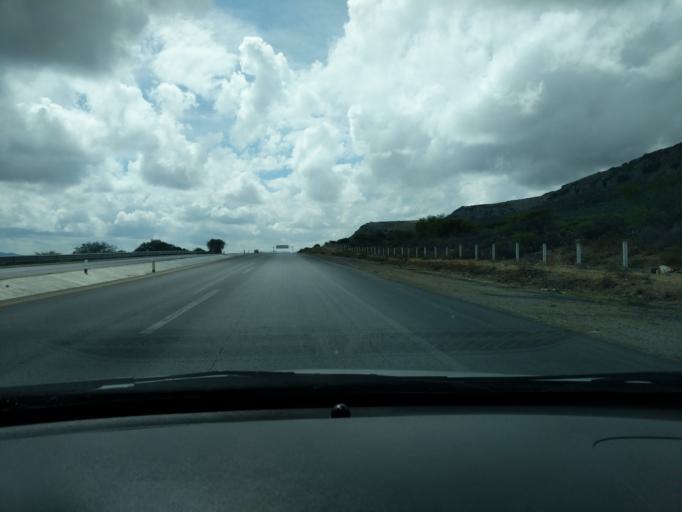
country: MX
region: Zacatecas
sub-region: Pinos
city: Santiago
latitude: 22.4007
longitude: -101.3763
